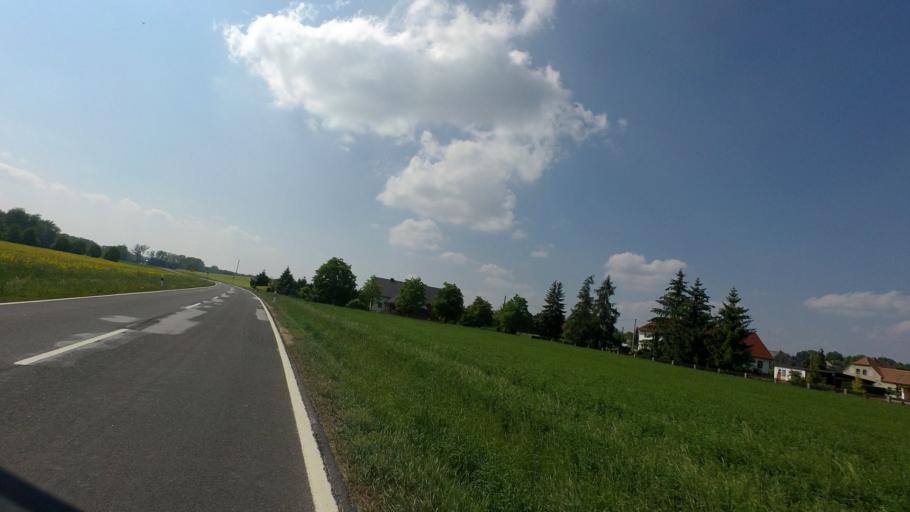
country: DE
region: Saxony
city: Hochkirch
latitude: 51.1919
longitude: 14.6021
